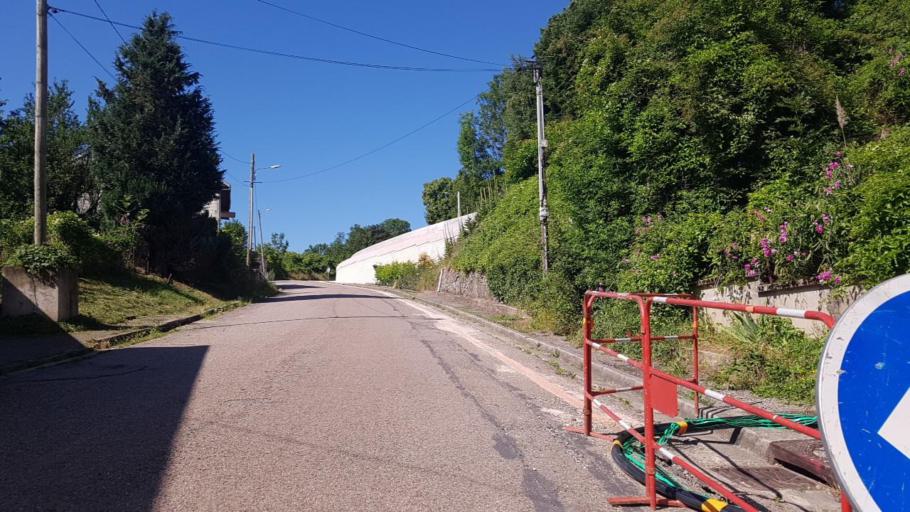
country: FR
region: Lorraine
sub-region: Departement de Meurthe-et-Moselle
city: Foug
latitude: 48.6859
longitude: 5.7850
